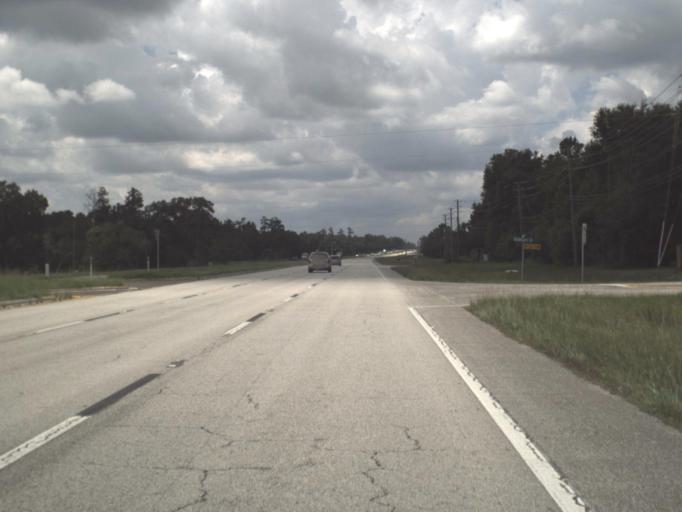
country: US
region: Florida
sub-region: Hernando County
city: South Brooksville
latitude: 28.4983
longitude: -82.4260
